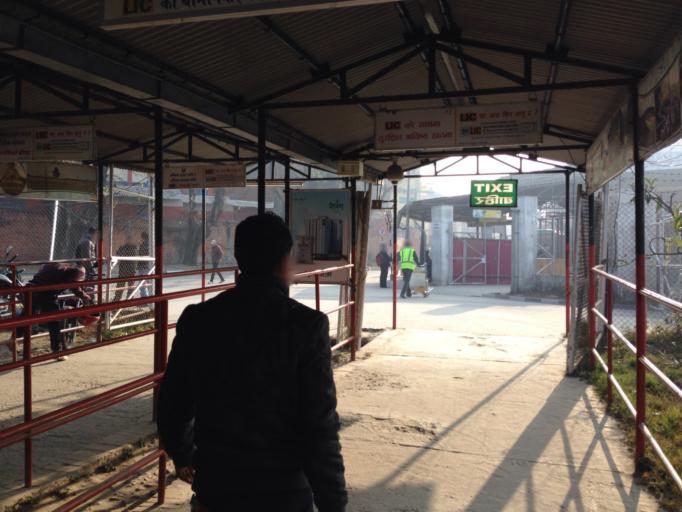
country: NP
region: Central Region
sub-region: Bagmati Zone
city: Kathmandu
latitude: 27.7030
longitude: 85.3582
